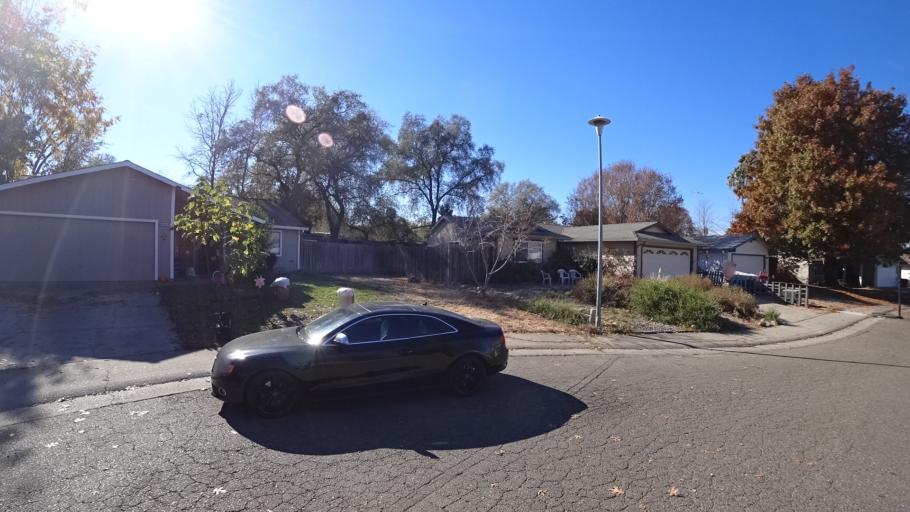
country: US
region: California
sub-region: Sacramento County
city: Antelope
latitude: 38.7206
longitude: -121.3094
